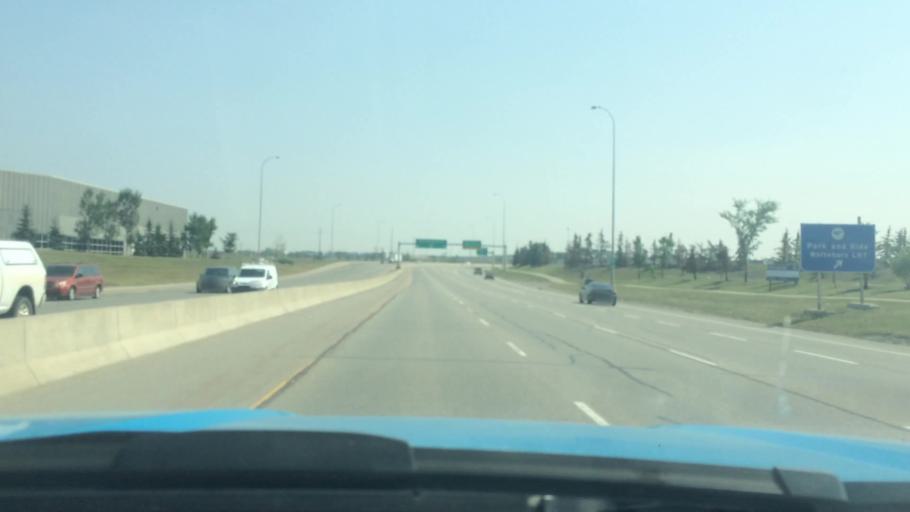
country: CA
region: Alberta
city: Calgary
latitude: 51.0939
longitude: -113.9952
